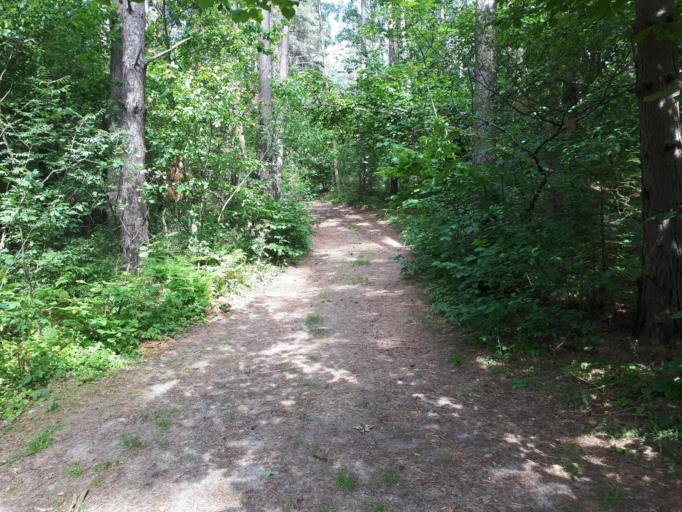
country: LT
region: Alytaus apskritis
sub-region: Alytaus rajonas
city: Daugai
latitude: 54.2256
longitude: 24.1806
